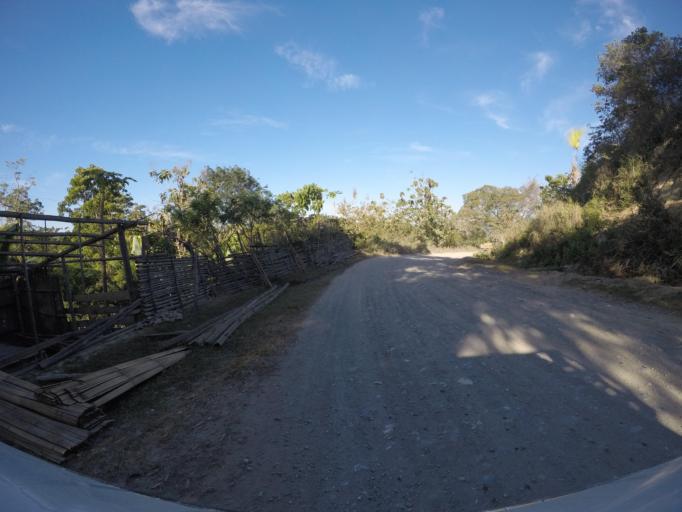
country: TL
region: Viqueque
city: Viqueque
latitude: -8.8663
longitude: 126.3344
